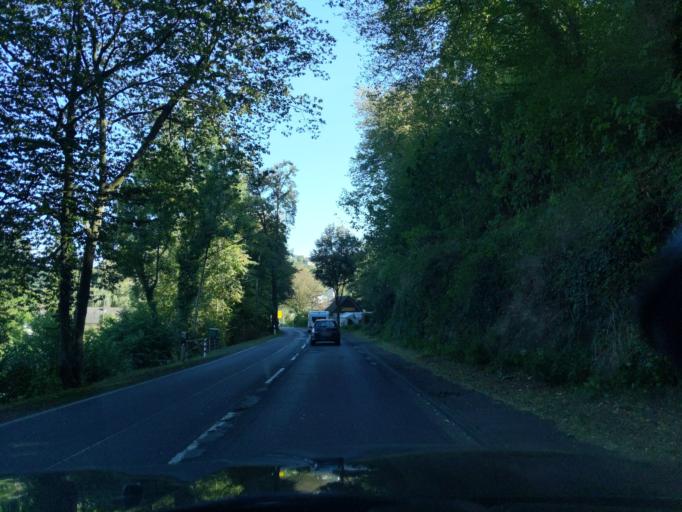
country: DE
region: North Rhine-Westphalia
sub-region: Regierungsbezirk Koln
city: Hennef
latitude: 50.7657
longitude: 7.3516
